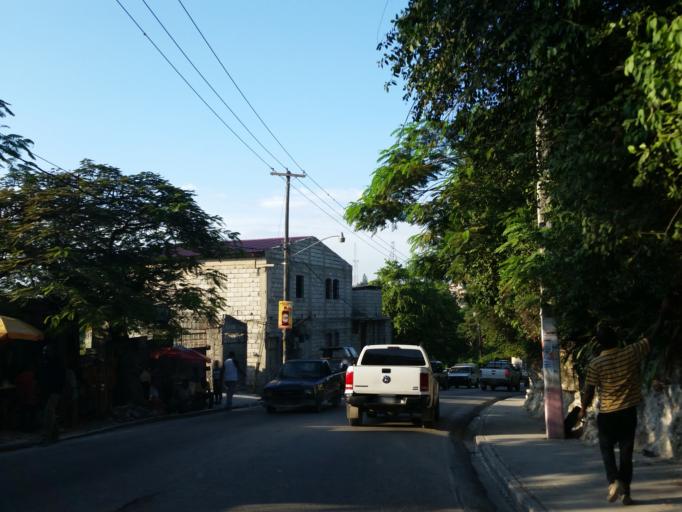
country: HT
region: Ouest
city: Petionville
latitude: 18.5202
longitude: -72.2930
